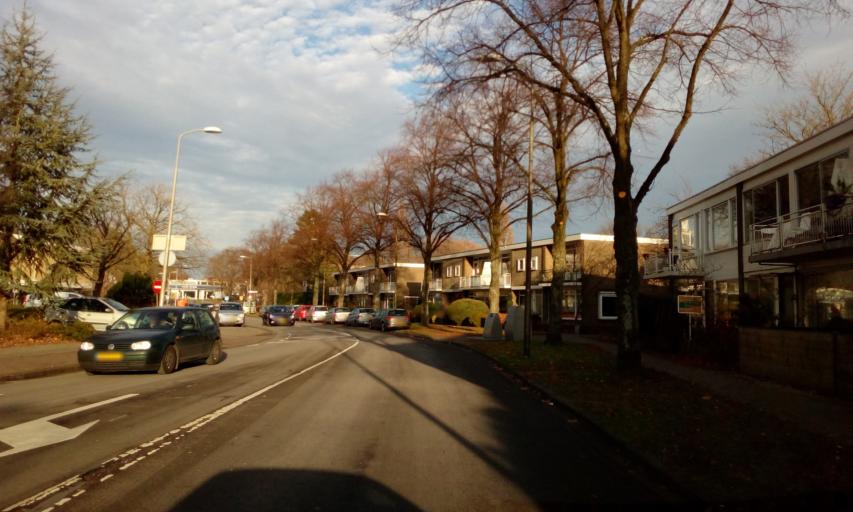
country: NL
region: South Holland
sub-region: Gemeente Zoetermeer
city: Zoetermeer
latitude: 52.0540
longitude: 4.4943
